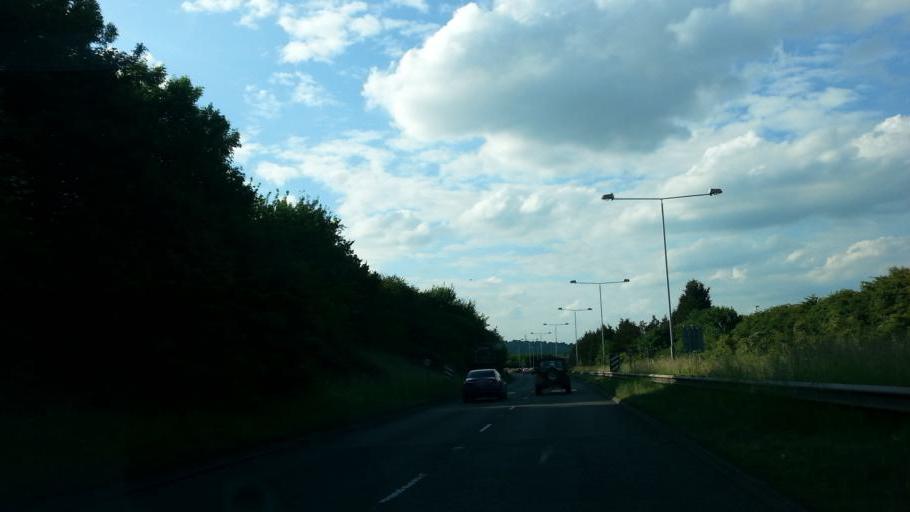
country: GB
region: England
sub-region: Nottinghamshire
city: West Bridgford
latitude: 52.9290
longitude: -1.0995
